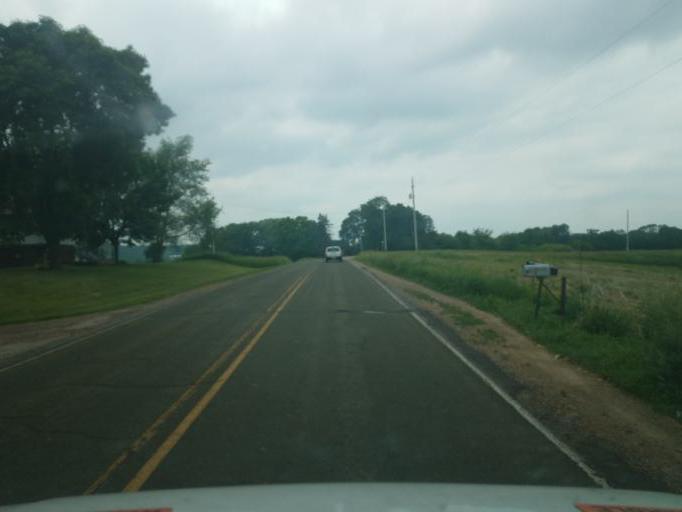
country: US
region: Wisconsin
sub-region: Vernon County
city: Hillsboro
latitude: 43.6478
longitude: -90.2651
